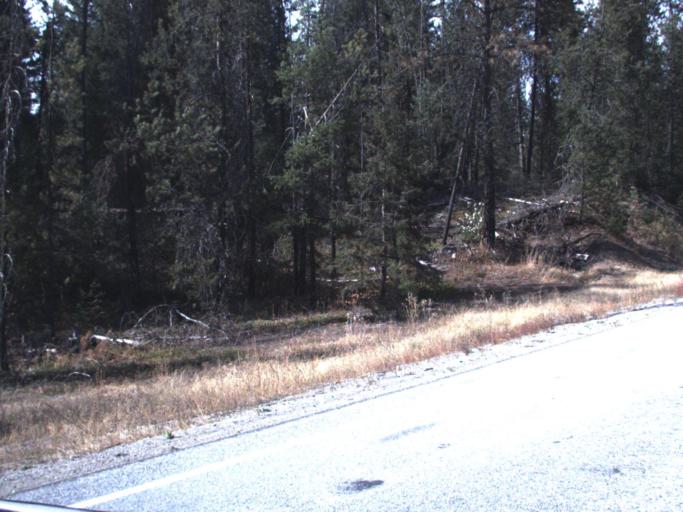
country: US
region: Washington
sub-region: Pend Oreille County
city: Newport
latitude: 48.1217
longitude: -117.2729
